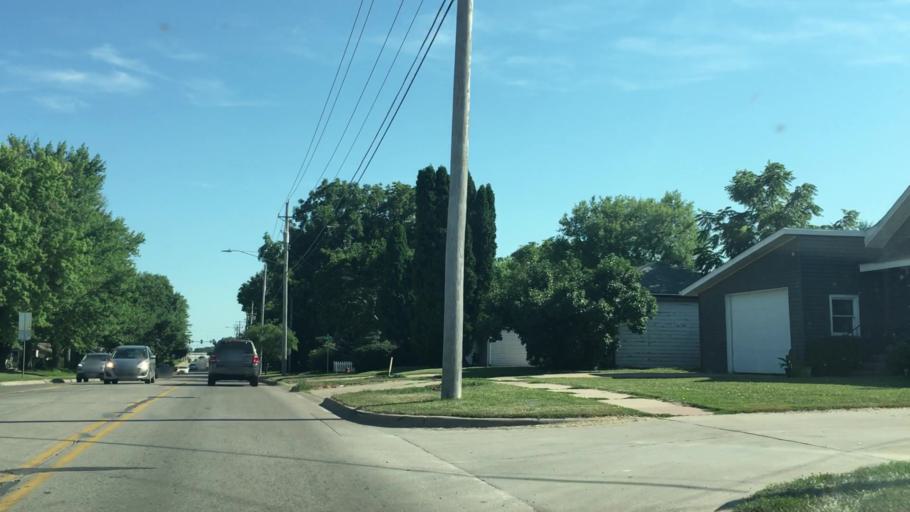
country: US
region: Iowa
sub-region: Johnson County
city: Iowa City
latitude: 41.6491
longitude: -91.5021
